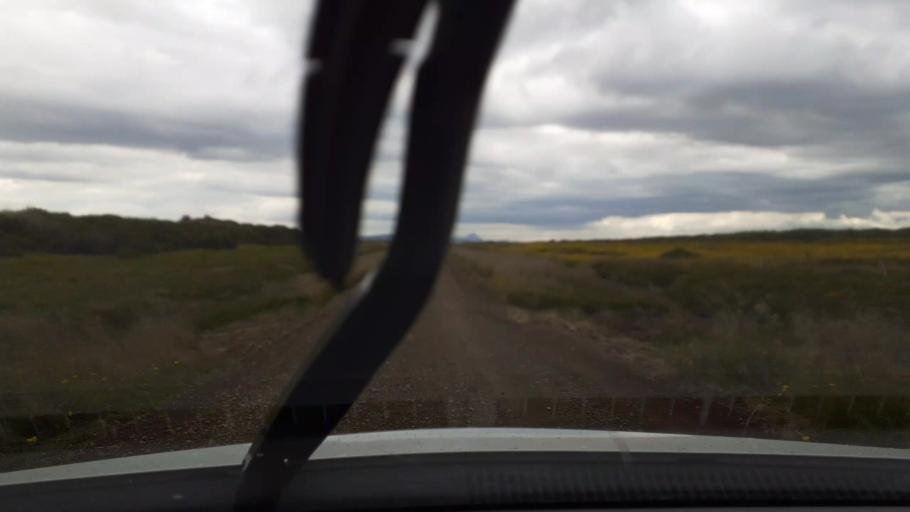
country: IS
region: West
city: Borgarnes
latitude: 64.6356
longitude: -21.9120
